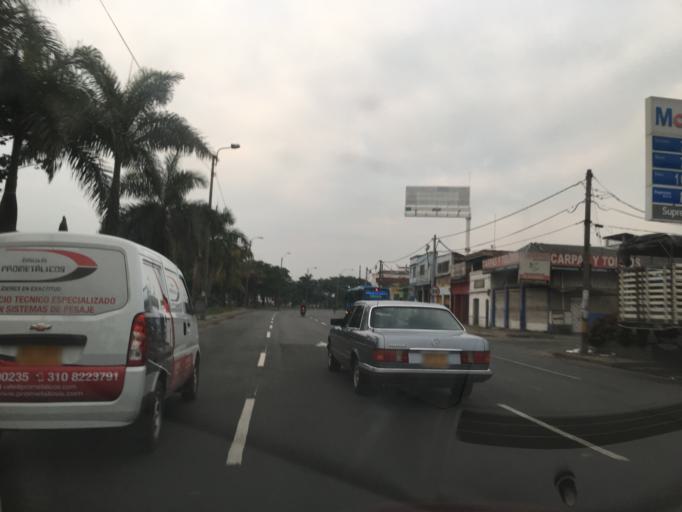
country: CO
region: Valle del Cauca
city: Cali
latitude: 3.4498
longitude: -76.5184
